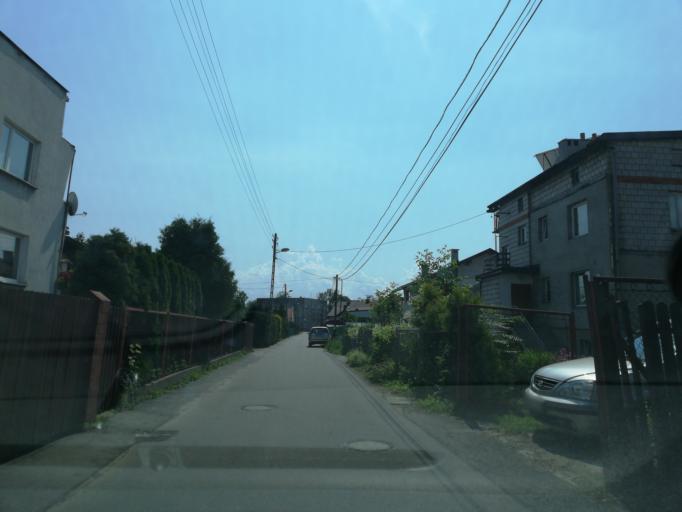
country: PL
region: Lesser Poland Voivodeship
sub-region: Powiat nowosadecki
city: Chelmiec
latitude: 49.6306
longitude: 20.6798
